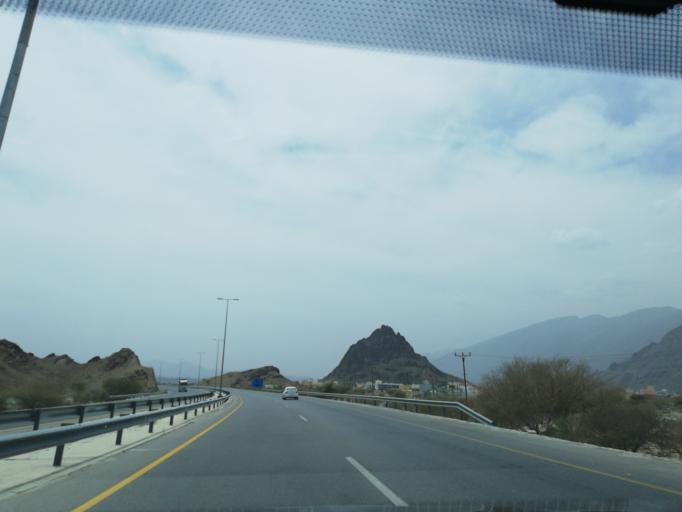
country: OM
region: Muhafazat ad Dakhiliyah
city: Sufalat Sama'il
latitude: 23.2897
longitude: 57.9364
